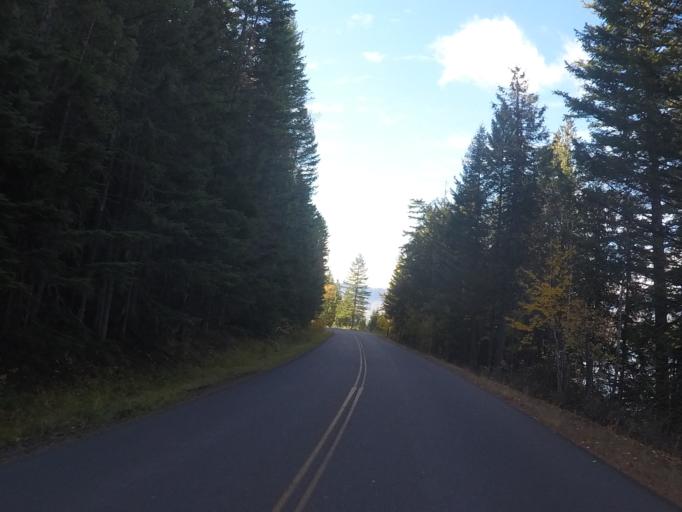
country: US
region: Montana
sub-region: Flathead County
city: Columbia Falls
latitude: 48.5725
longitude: -113.9138
